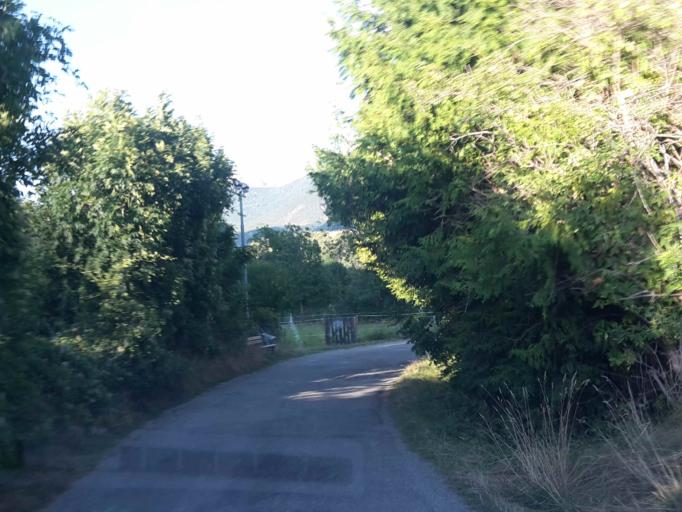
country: FR
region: Provence-Alpes-Cote d'Azur
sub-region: Departement des Hautes-Alpes
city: Embrun
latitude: 44.5620
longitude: 6.5006
